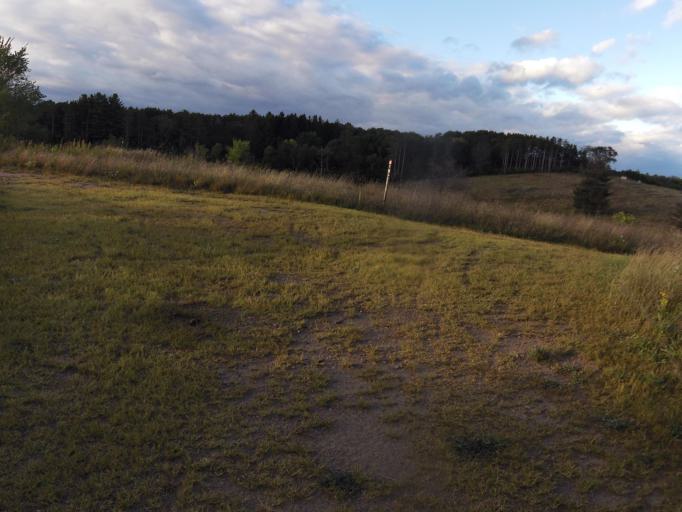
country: US
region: Minnesota
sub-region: Washington County
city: Lake Saint Croix Beach
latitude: 44.9365
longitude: -92.7870
